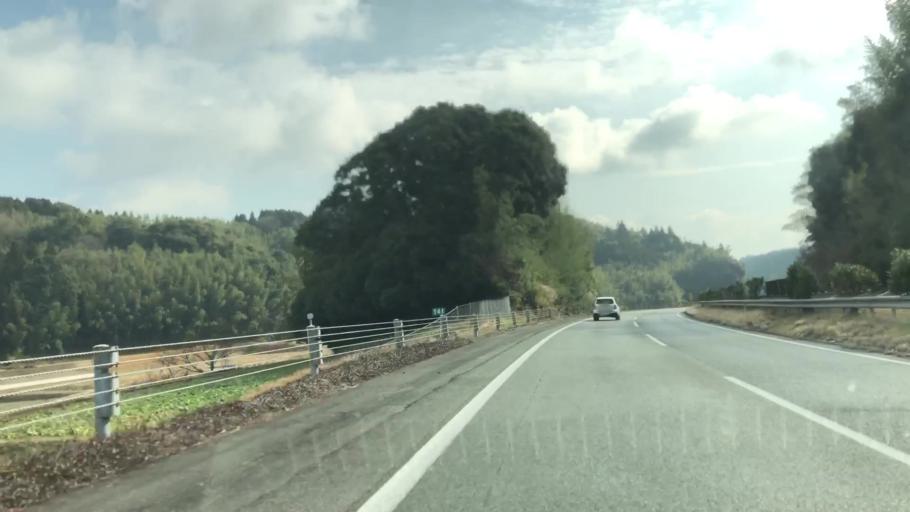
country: JP
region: Kumamoto
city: Yamaga
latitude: 33.0284
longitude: 130.5763
